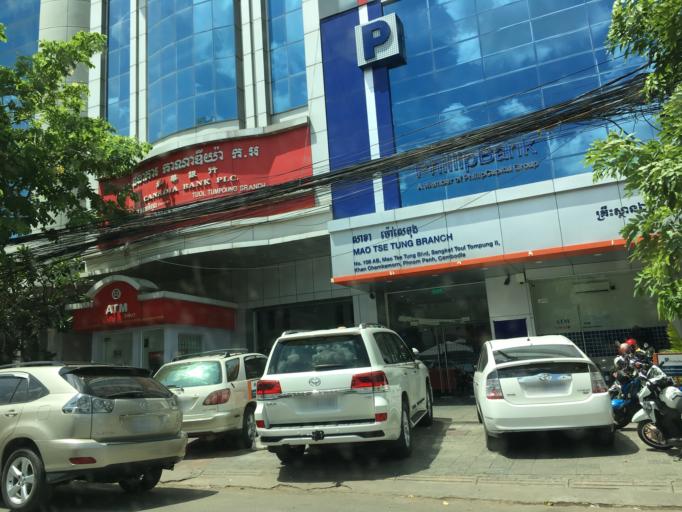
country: KH
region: Phnom Penh
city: Phnom Penh
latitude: 11.5441
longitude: 104.9122
